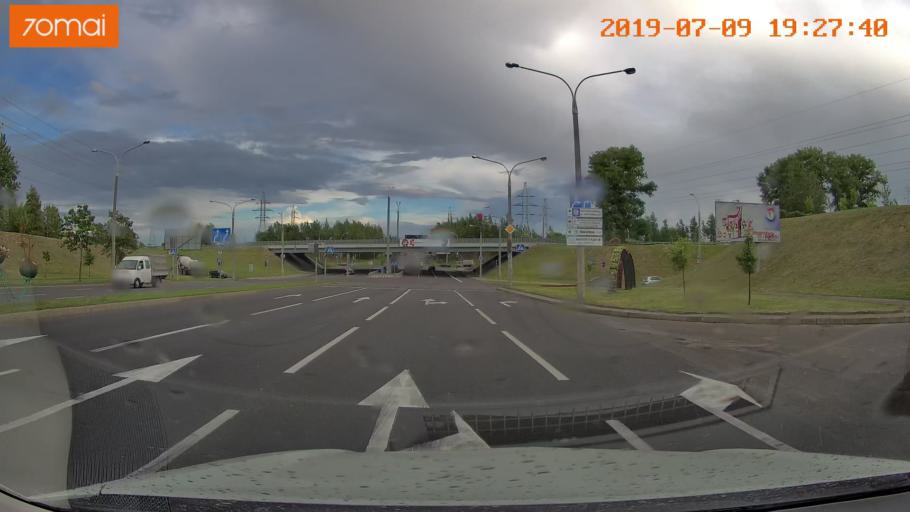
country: BY
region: Minsk
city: Syenitsa
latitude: 53.8343
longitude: 27.5746
